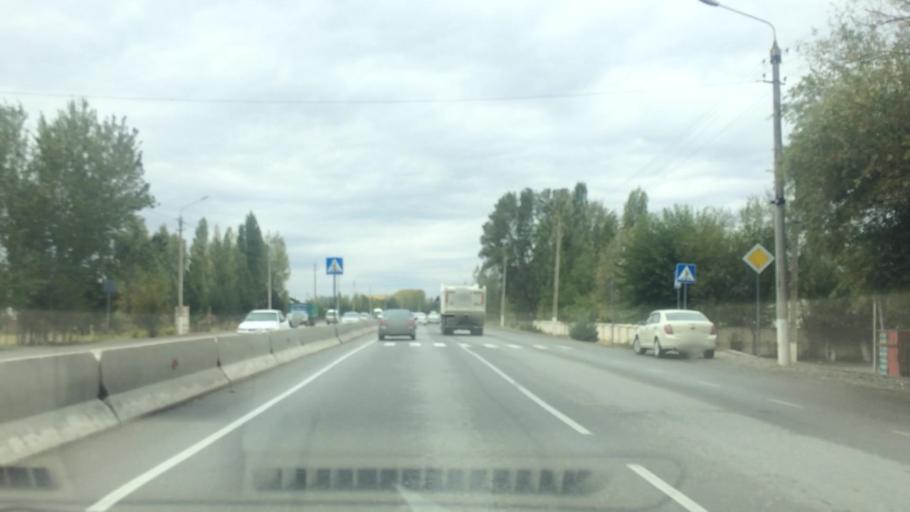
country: UZ
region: Jizzax
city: Jizzax
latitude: 39.9931
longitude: 67.5849
